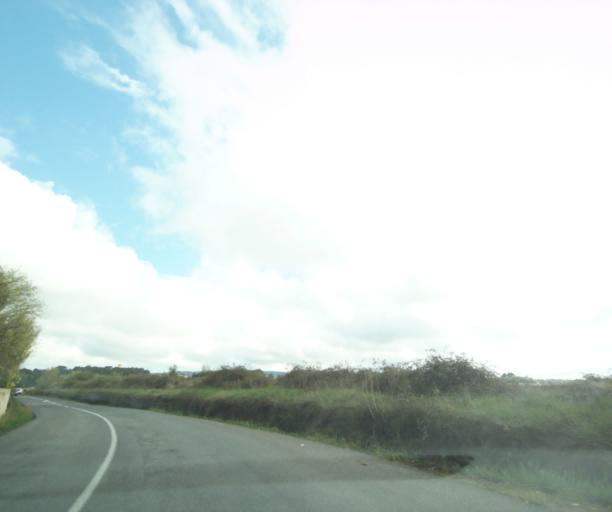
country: FR
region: Languedoc-Roussillon
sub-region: Departement de l'Herault
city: Saussan
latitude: 43.5785
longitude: 3.7681
